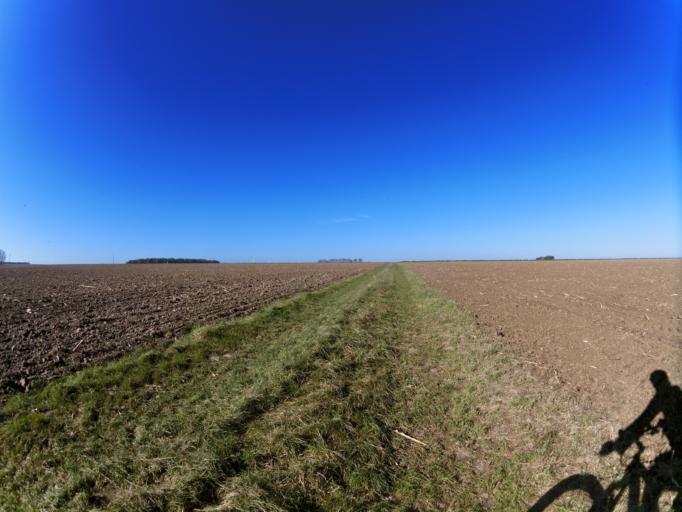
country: DE
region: Bavaria
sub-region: Regierungsbezirk Unterfranken
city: Giebelstadt
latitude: 49.6634
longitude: 9.9328
